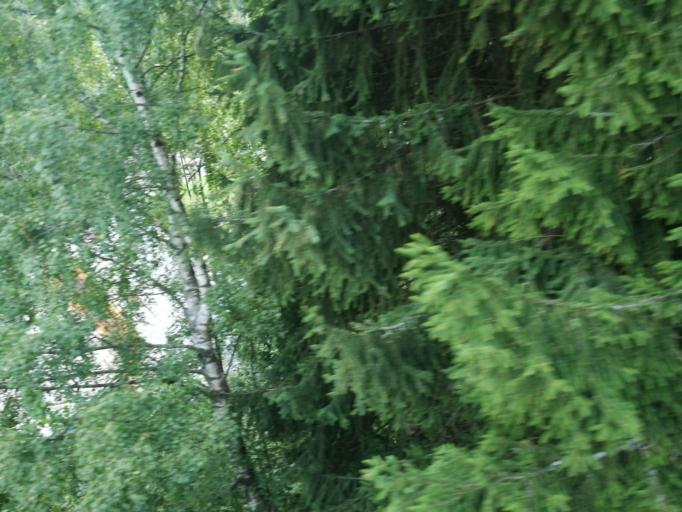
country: CZ
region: Kralovehradecky
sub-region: Okres Trutnov
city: Svoboda nad Upou
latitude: 50.6335
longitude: 15.7678
